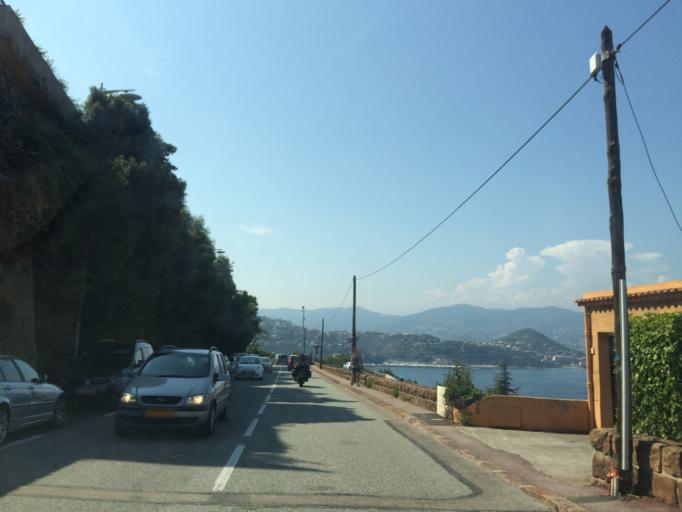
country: FR
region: Provence-Alpes-Cote d'Azur
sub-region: Departement des Alpes-Maritimes
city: Theoule-sur-Mer
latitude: 43.5045
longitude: 6.9532
